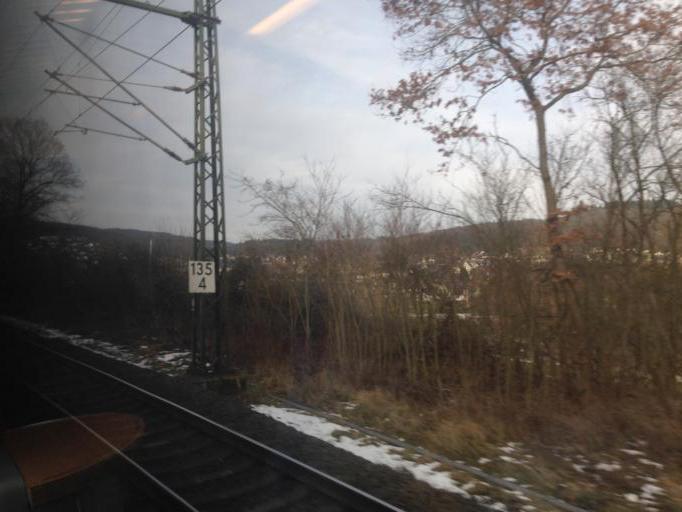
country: DE
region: Hesse
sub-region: Regierungsbezirk Giessen
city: Sinn
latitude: 50.6459
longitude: 8.3269
